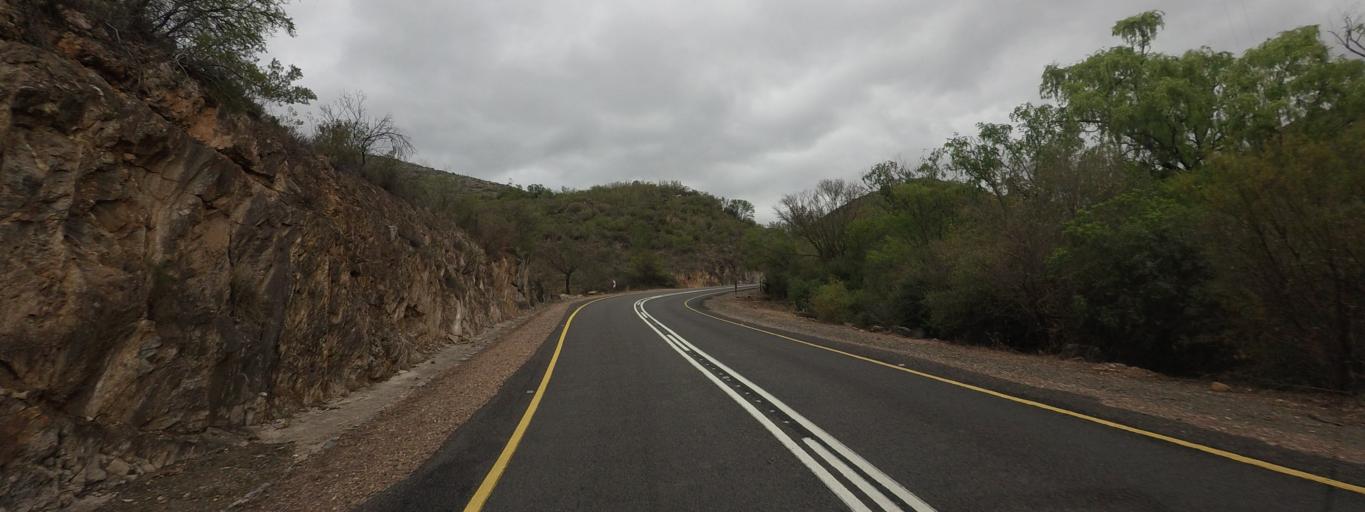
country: ZA
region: Western Cape
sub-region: Eden District Municipality
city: Oudtshoorn
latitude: -33.3961
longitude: 22.2156
